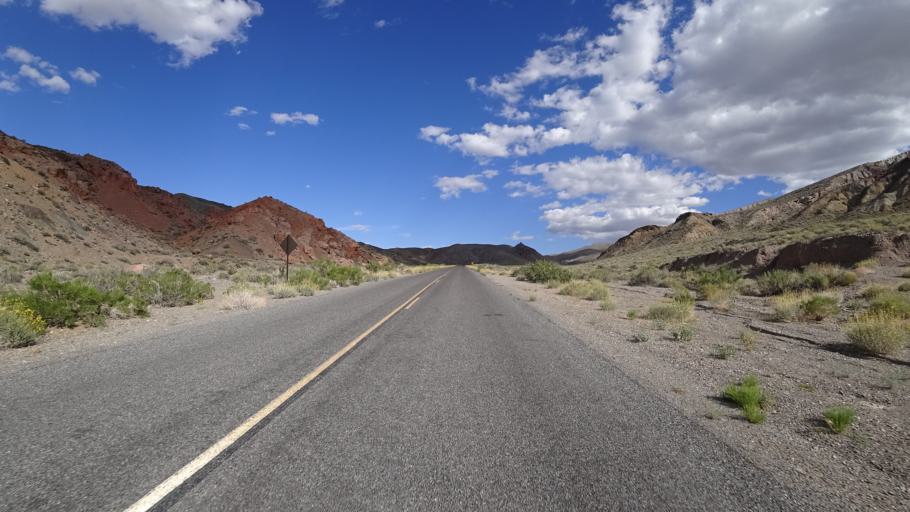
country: US
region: Nevada
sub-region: Nye County
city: Beatty
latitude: 36.4244
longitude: -117.1914
